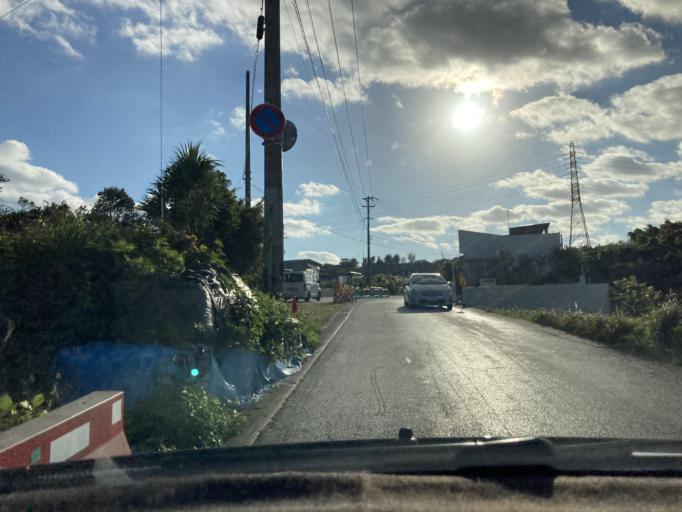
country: JP
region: Okinawa
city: Gushikawa
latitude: 26.3569
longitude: 127.8532
